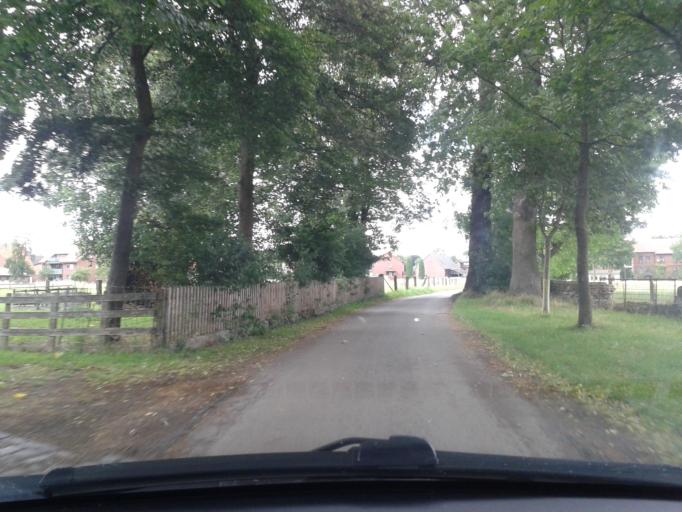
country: DE
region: North Rhine-Westphalia
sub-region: Regierungsbezirk Detmold
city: Hovelhof
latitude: 51.7363
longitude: 8.6655
